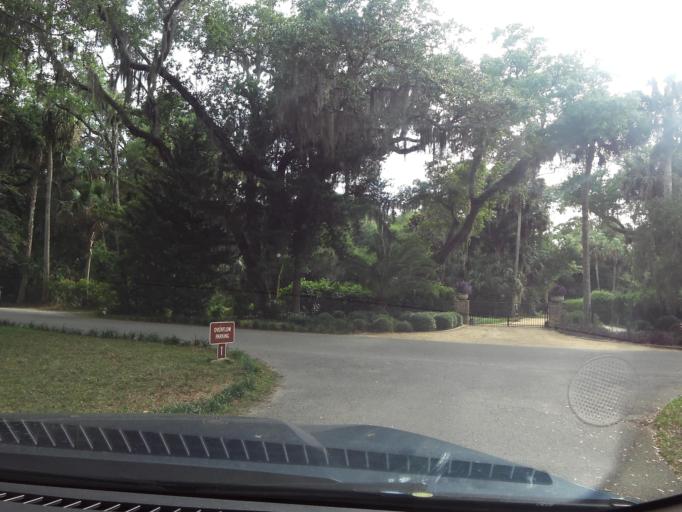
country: US
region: Florida
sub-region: Flagler County
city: Palm Coast
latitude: 29.6307
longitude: -81.2073
